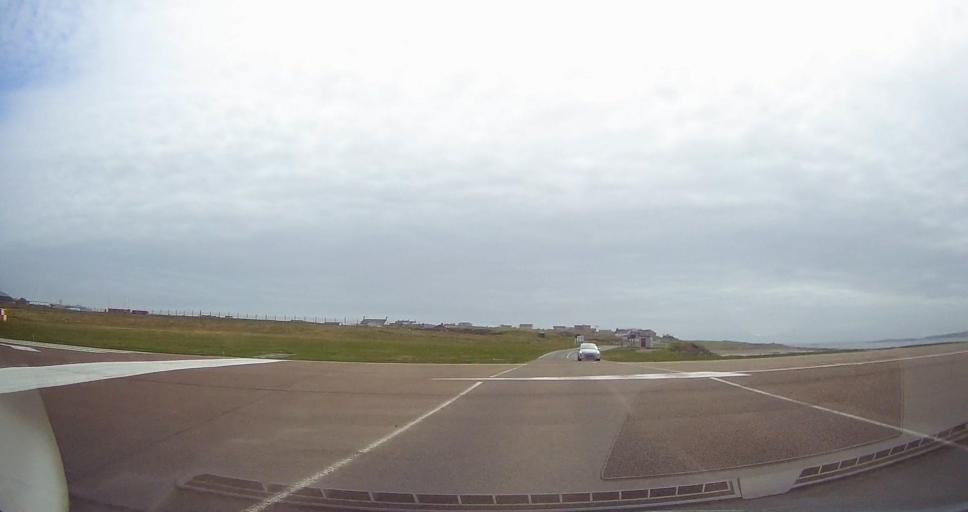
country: GB
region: Scotland
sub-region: Shetland Islands
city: Sandwick
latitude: 59.8813
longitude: -1.3054
